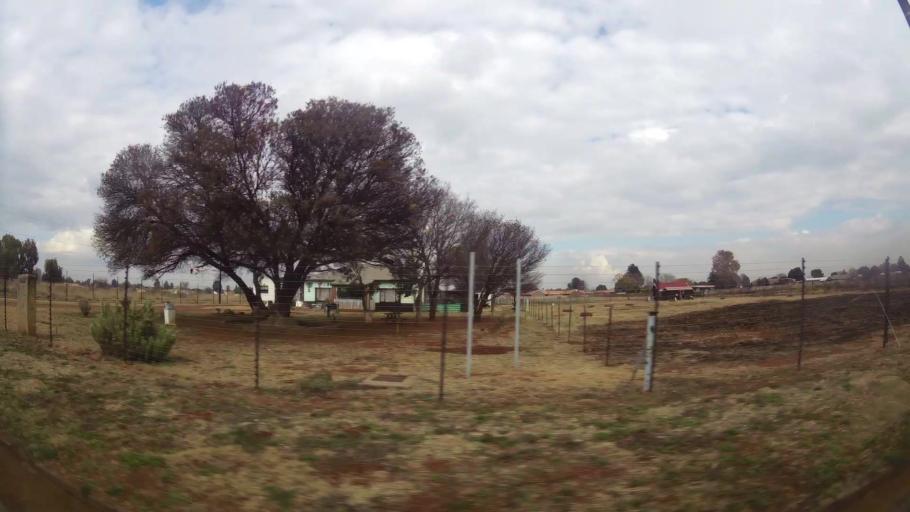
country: ZA
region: Gauteng
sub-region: Sedibeng District Municipality
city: Meyerton
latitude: -26.5958
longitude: 27.9969
